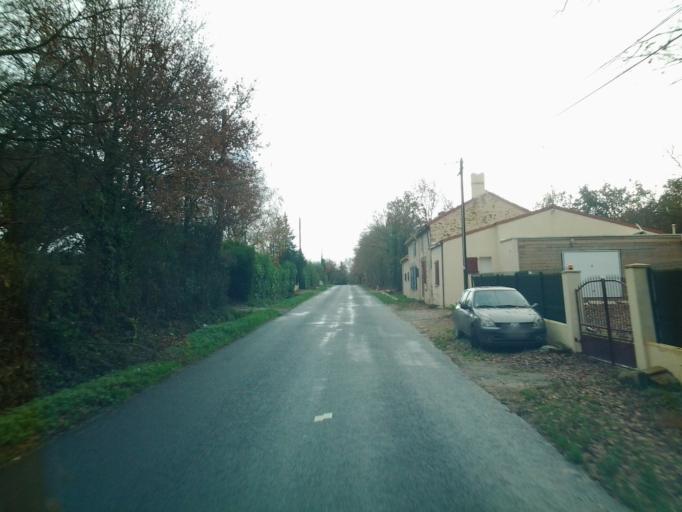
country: FR
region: Pays de la Loire
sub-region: Departement de la Vendee
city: Nesmy
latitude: 46.6463
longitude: -1.3733
